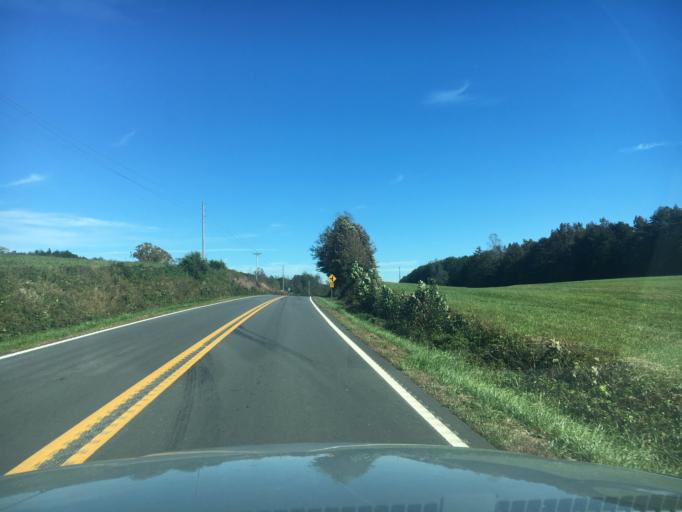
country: US
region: North Carolina
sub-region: Burke County
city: Glen Alpine
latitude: 35.6348
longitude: -81.7960
